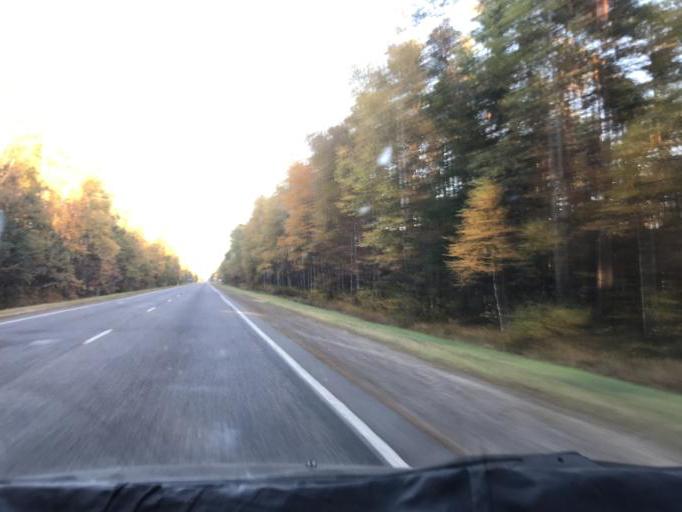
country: BY
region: Gomel
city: Pyetrykaw
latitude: 52.2748
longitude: 28.1887
